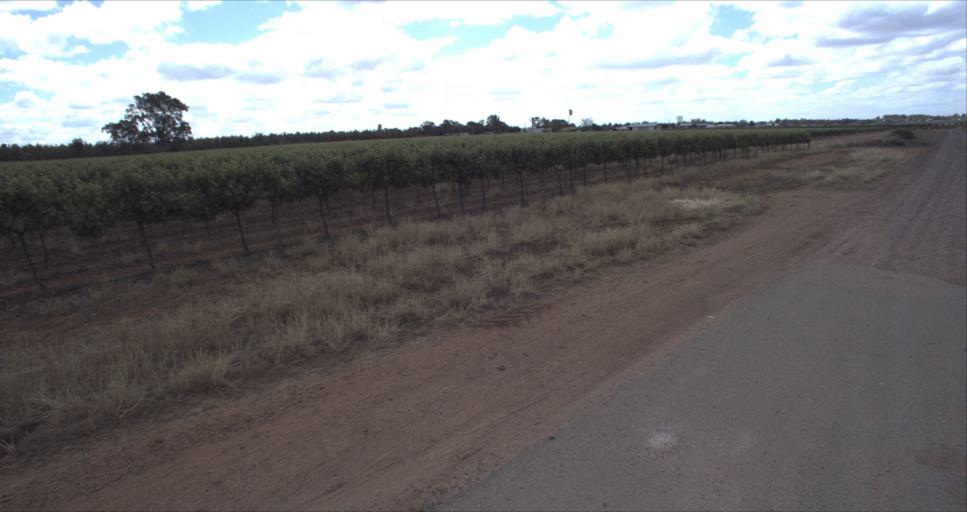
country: AU
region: New South Wales
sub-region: Leeton
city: Leeton
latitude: -34.5768
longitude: 146.4008
